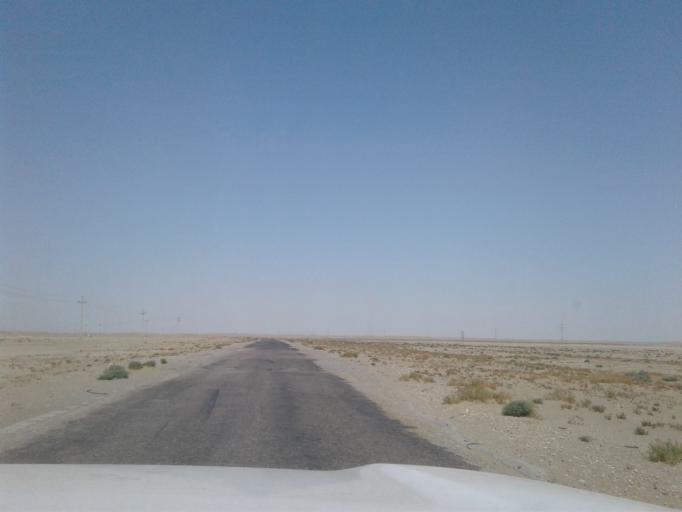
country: TM
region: Balkan
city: Gumdag
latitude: 38.3841
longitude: 54.3962
